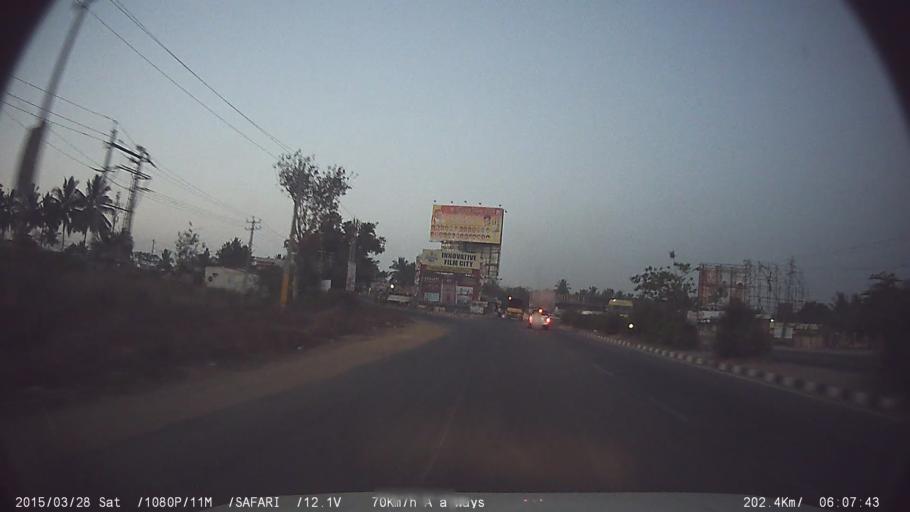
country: IN
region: Karnataka
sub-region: Ramanagara
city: Ramanagaram
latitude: 12.8036
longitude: 77.3984
